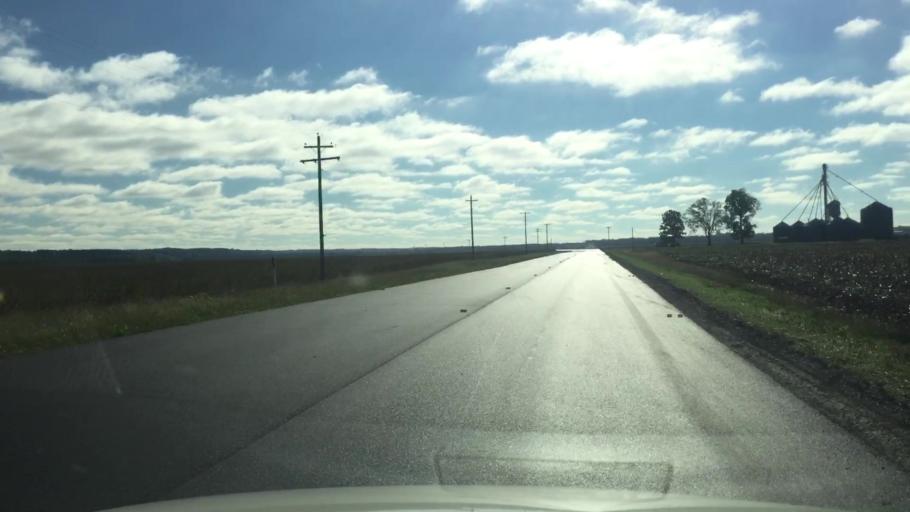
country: US
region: Missouri
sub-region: Howard County
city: New Franklin
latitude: 38.9994
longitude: -92.6739
